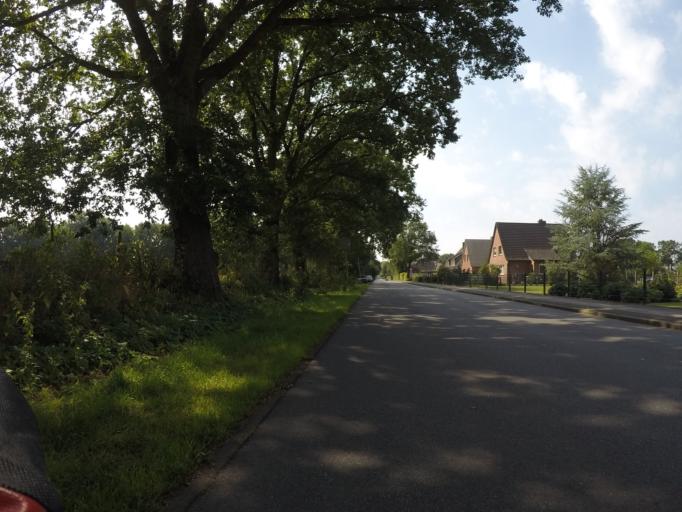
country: DE
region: Schleswig-Holstein
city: Tangstedt
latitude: 53.7021
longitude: 10.0514
